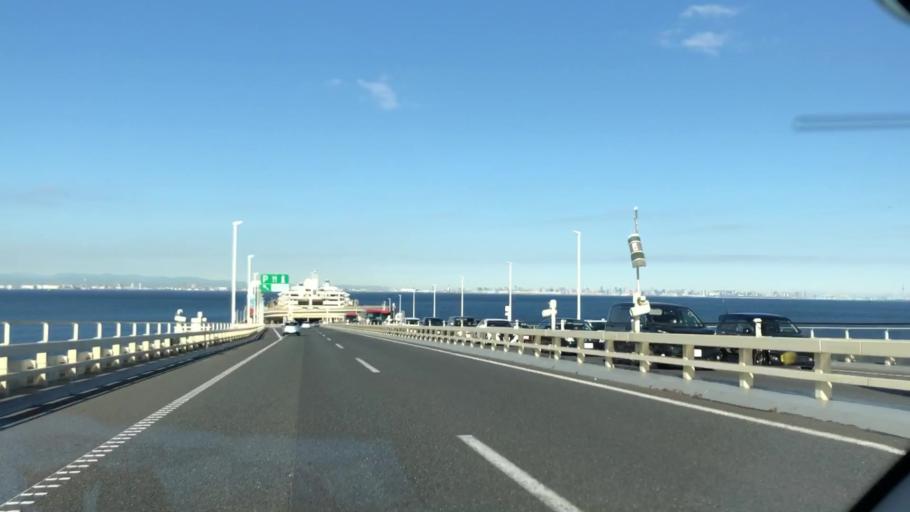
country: JP
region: Chiba
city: Kisarazu
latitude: 35.4587
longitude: 139.8824
